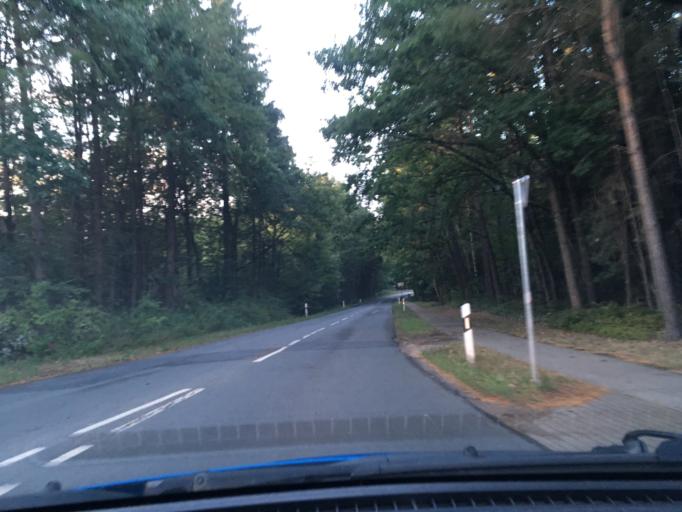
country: DE
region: Lower Saxony
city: Fassberg
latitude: 52.8831
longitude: 10.1422
